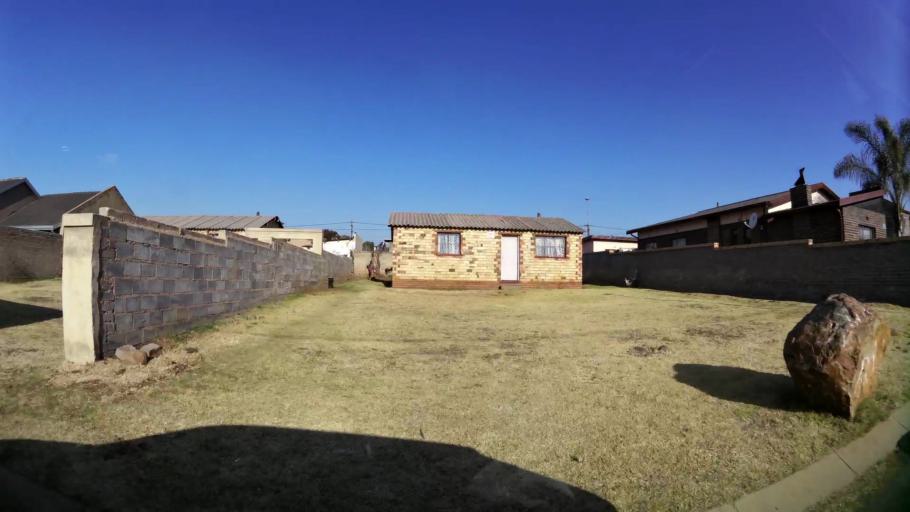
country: ZA
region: Gauteng
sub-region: City of Johannesburg Metropolitan Municipality
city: Soweto
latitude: -26.2656
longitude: 27.8696
